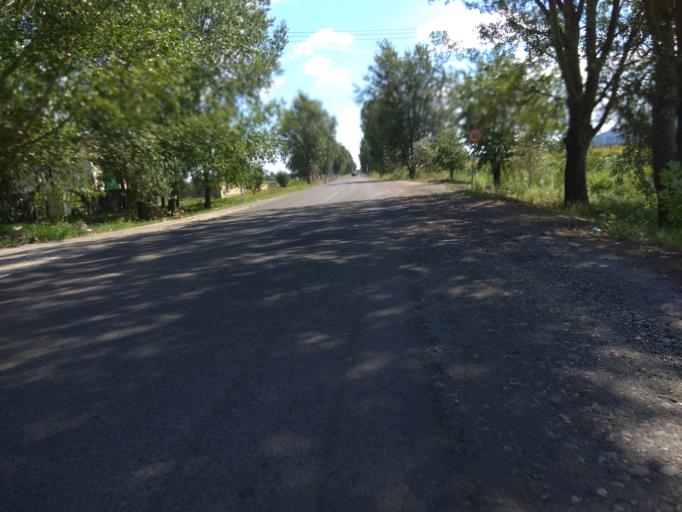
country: HU
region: Borsod-Abauj-Zemplen
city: Sajokaza
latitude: 48.2666
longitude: 20.5994
